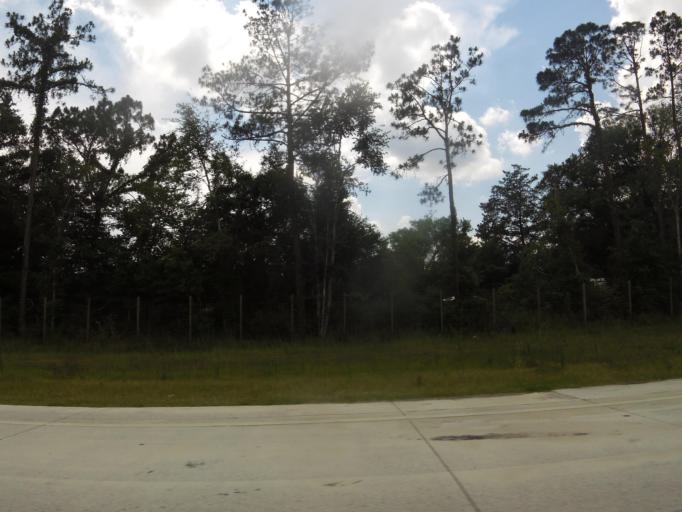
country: US
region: Florida
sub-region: Duval County
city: Baldwin
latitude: 30.3043
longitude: -81.9894
